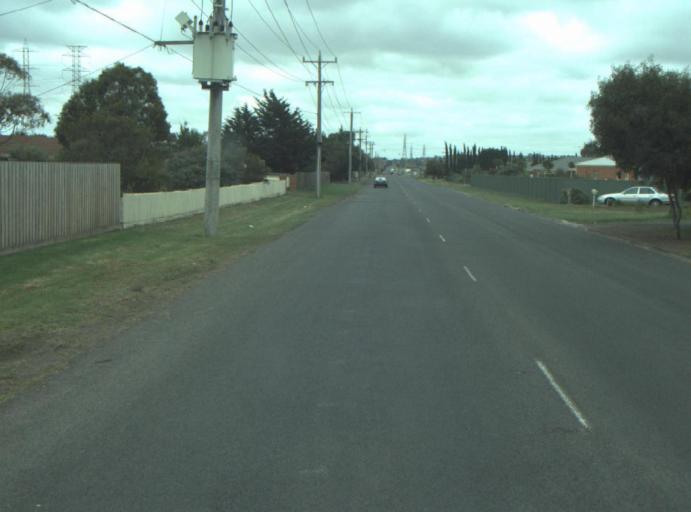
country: AU
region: Victoria
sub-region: Greater Geelong
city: Bell Post Hill
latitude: -38.0685
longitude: 144.3397
